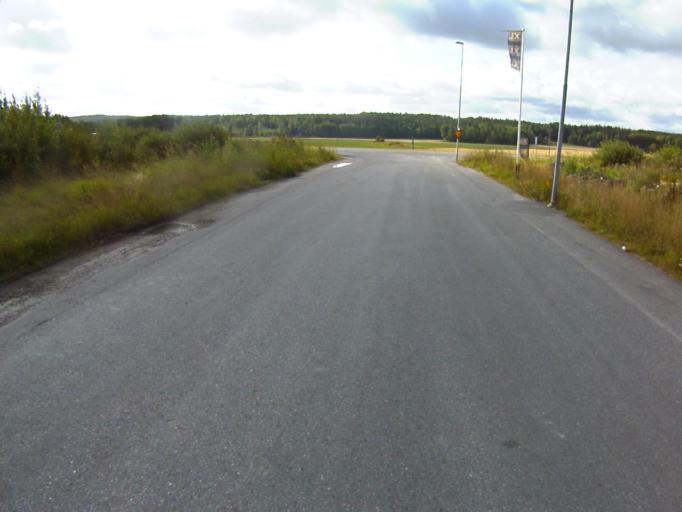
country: SE
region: Soedermanland
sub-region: Eskilstuna Kommun
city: Eskilstuna
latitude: 59.3774
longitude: 16.5808
